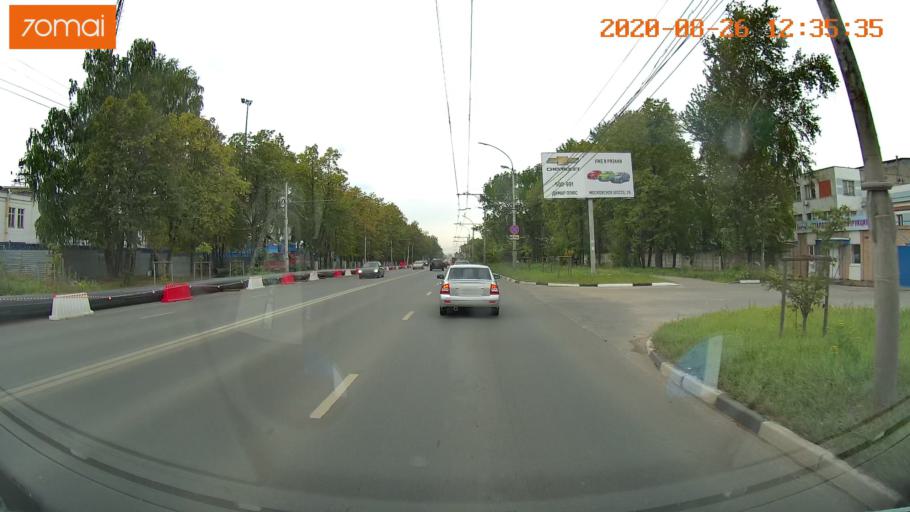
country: RU
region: Rjazan
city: Ryazan'
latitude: 54.5969
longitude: 39.7677
